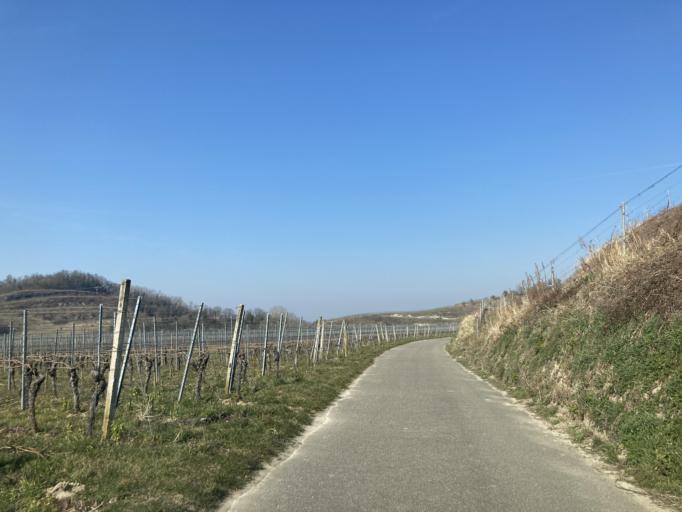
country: DE
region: Baden-Wuerttemberg
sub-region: Freiburg Region
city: Ihringen
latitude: 48.0684
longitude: 7.6393
